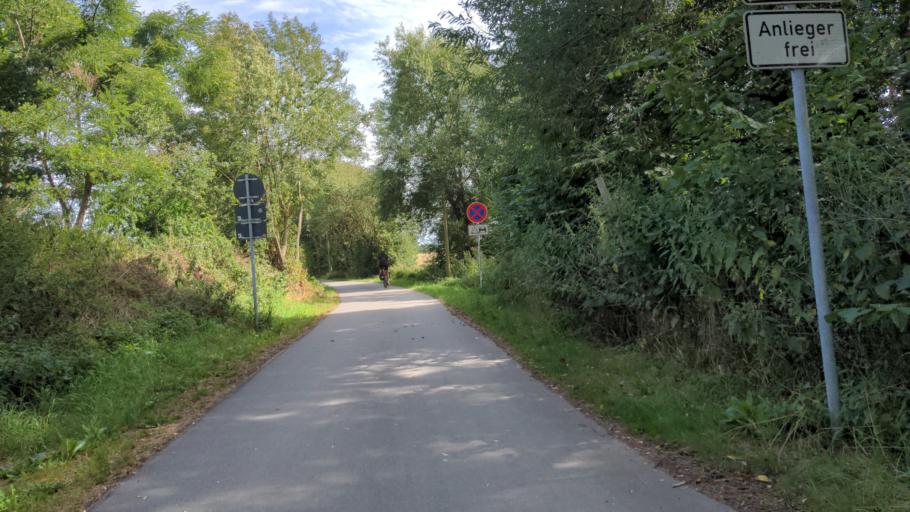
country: DE
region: Mecklenburg-Vorpommern
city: Kalkhorst
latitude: 54.0056
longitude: 11.0666
